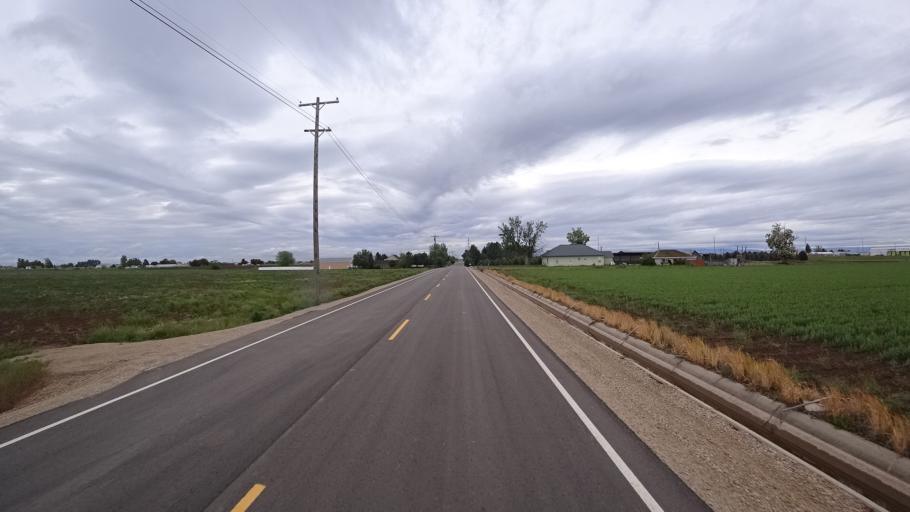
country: US
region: Idaho
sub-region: Ada County
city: Star
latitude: 43.6682
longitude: -116.5129
